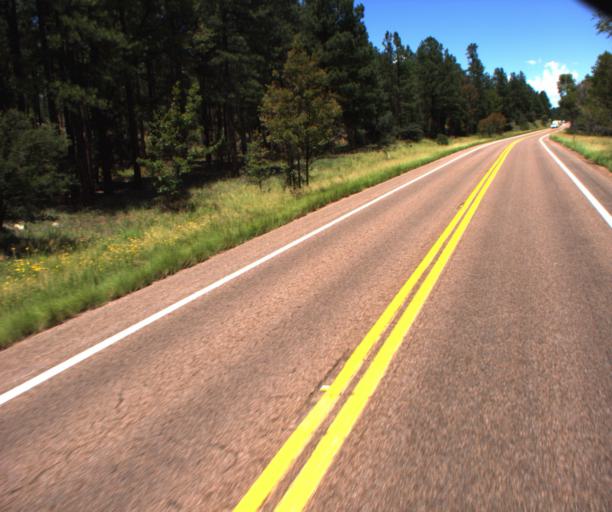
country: US
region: Arizona
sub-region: Navajo County
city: Lake of the Woods
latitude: 34.1489
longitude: -110.1038
